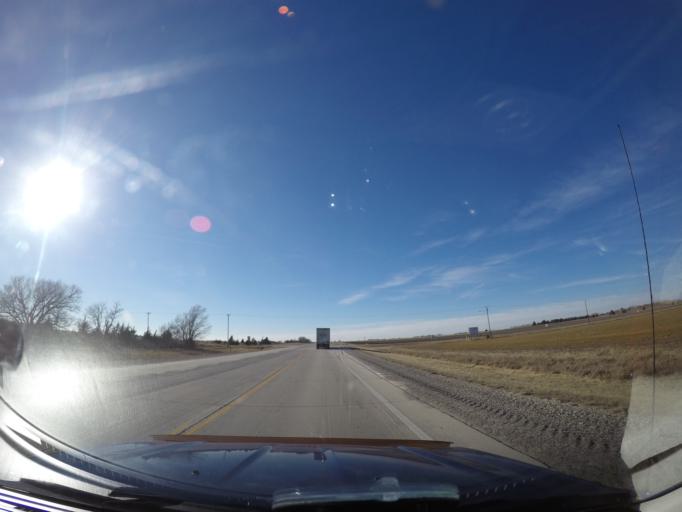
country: US
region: Kansas
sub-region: Marion County
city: Marion
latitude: 38.3558
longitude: -97.0940
